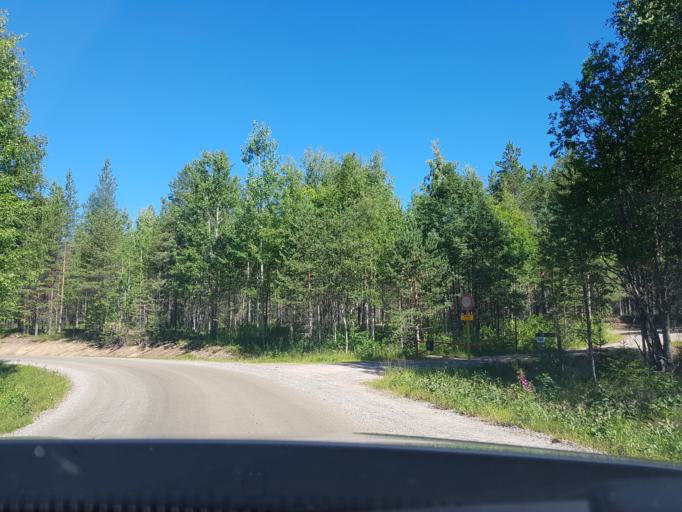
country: FI
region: Kainuu
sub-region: Kehys-Kainuu
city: Kuhmo
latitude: 64.1941
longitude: 29.6046
